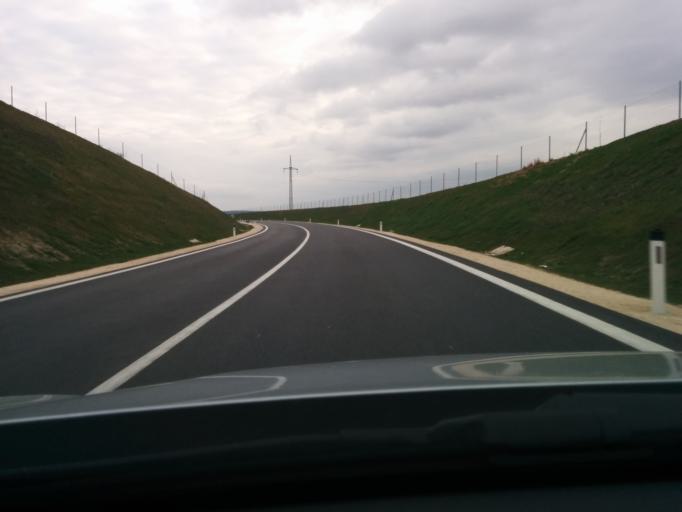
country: AT
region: Lower Austria
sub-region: Politischer Bezirk Mistelbach
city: Mistelbach
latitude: 48.5702
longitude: 16.5536
